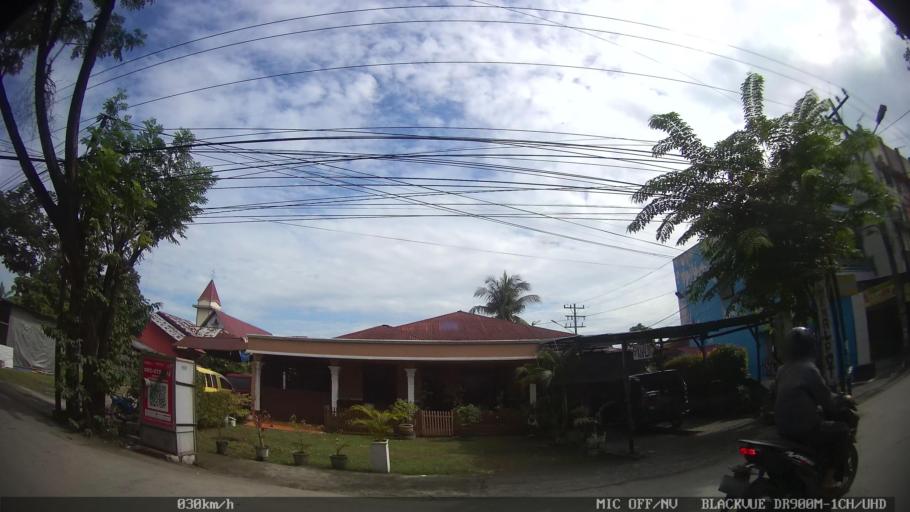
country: ID
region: North Sumatra
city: Sunggal
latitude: 3.6064
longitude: 98.6149
